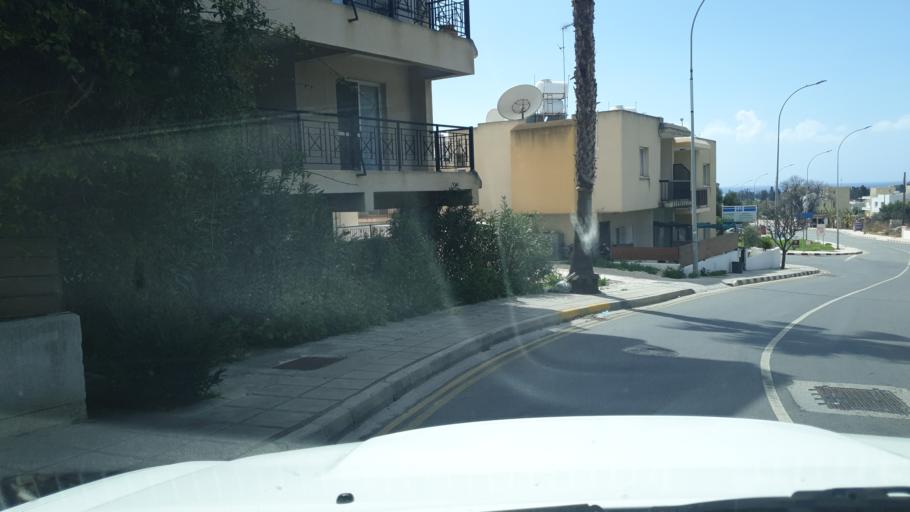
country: CY
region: Pafos
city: Paphos
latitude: 34.7568
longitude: 32.4572
